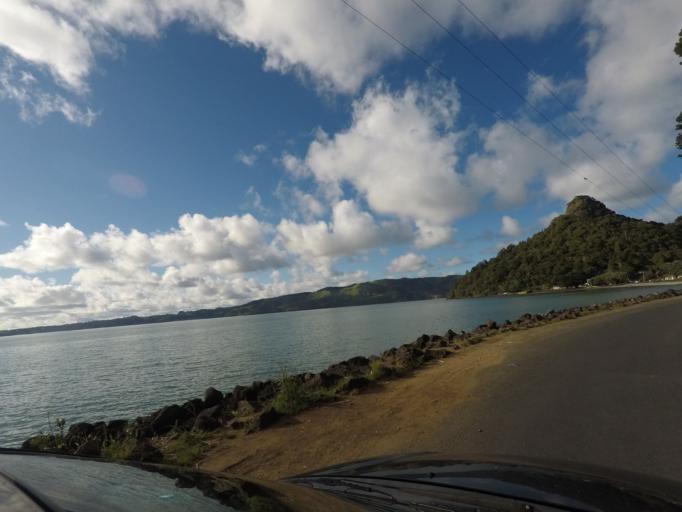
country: NZ
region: Auckland
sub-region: Auckland
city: Titirangi
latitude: -37.0132
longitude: 174.5604
